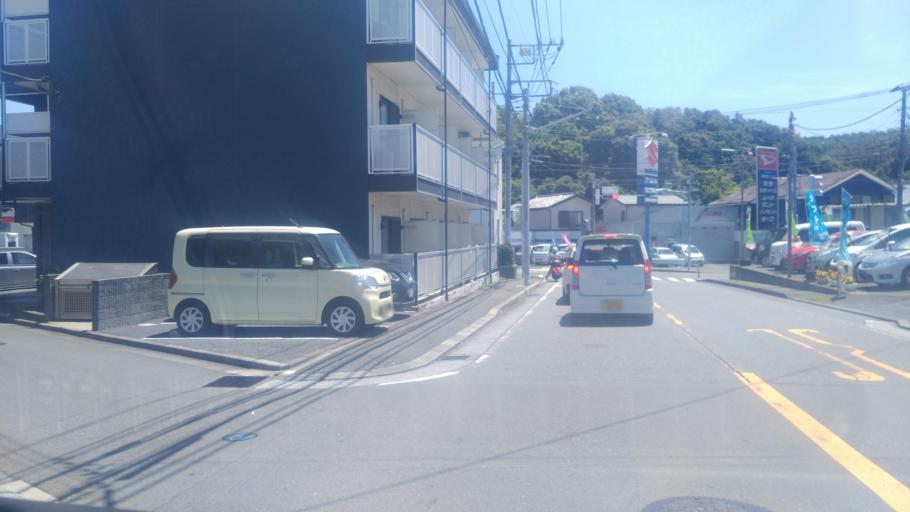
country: JP
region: Kanagawa
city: Fujisawa
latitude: 35.3910
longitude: 139.5101
